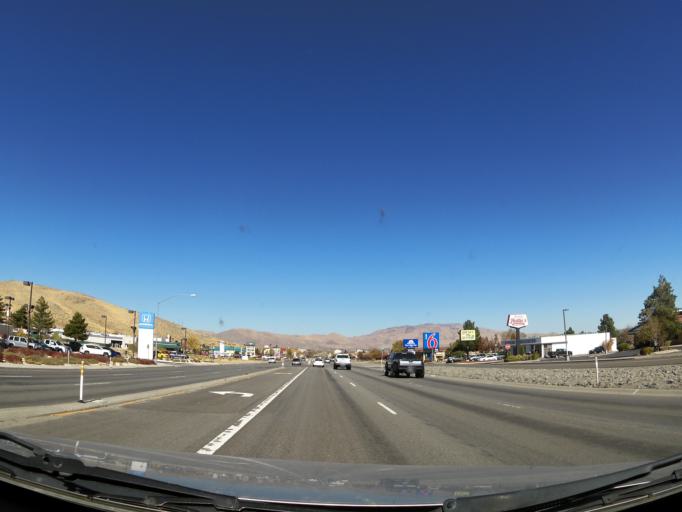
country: US
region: Nevada
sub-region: Carson City
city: Carson City
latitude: 39.1411
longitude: -119.7685
